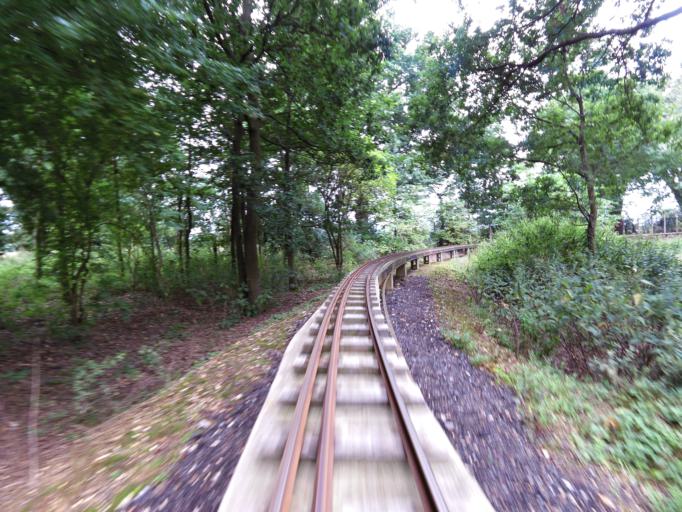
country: GB
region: England
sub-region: Hertfordshire
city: Hatfield
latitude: 51.7375
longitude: -0.2640
